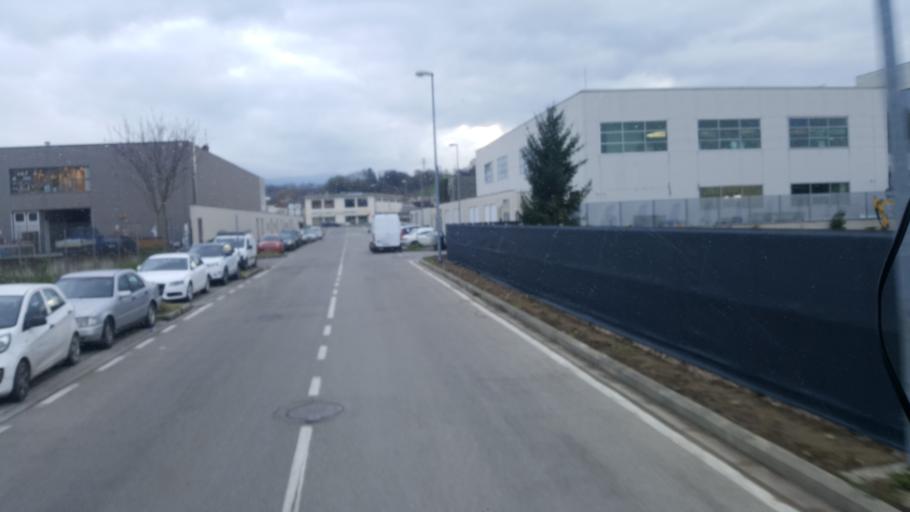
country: IT
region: Tuscany
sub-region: Province of Arezzo
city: Montevarchi
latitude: 43.5382
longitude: 11.5589
